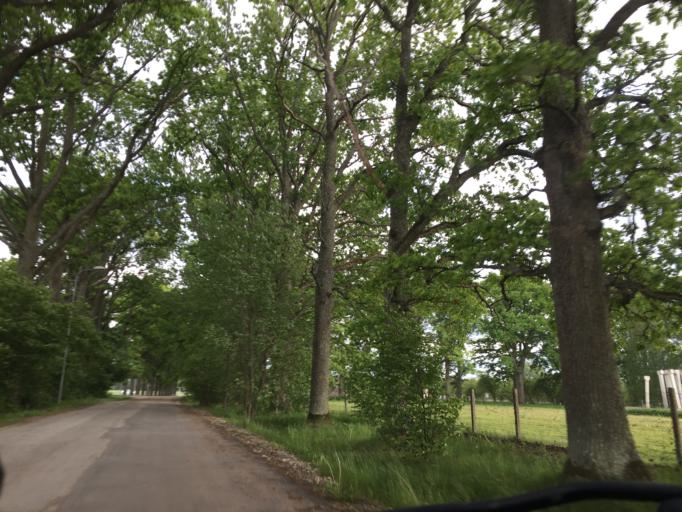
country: LV
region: Valmieras Rajons
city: Valmiera
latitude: 57.5528
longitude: 25.4174
